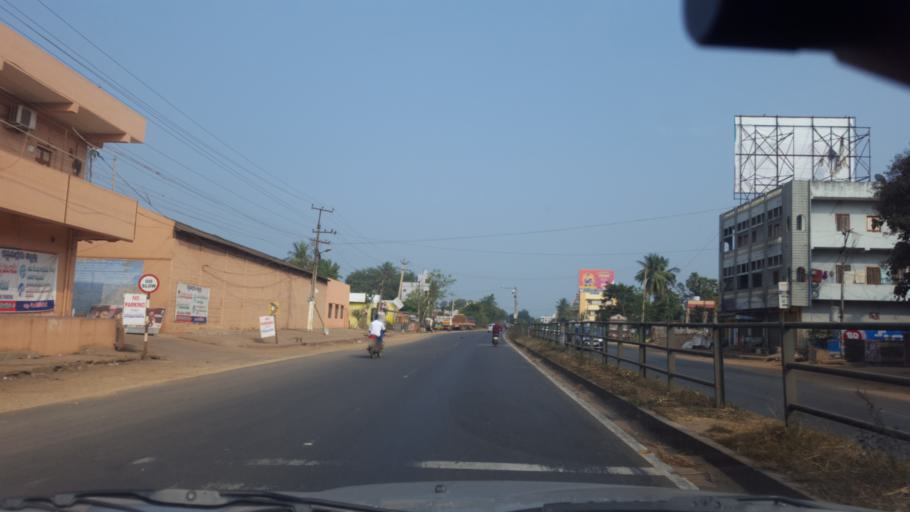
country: IN
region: Andhra Pradesh
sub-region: West Godavari
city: Eluru
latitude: 16.6365
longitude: 80.9762
